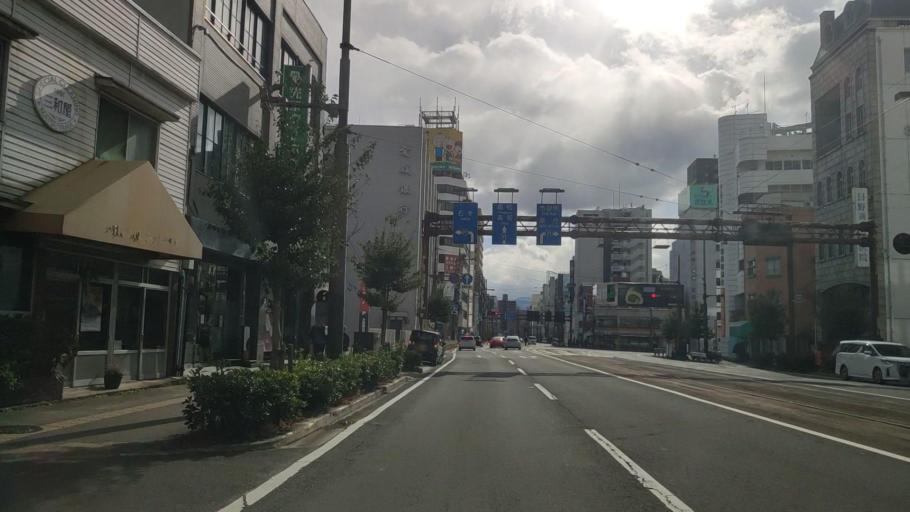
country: JP
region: Ehime
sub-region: Shikoku-chuo Shi
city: Matsuyama
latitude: 33.8428
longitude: 132.7755
